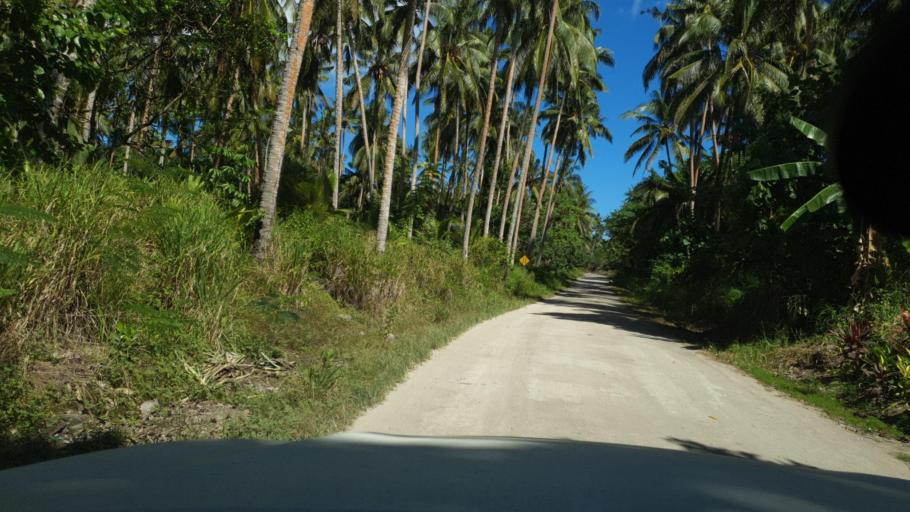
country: SB
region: Guadalcanal
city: Honiara
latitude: -9.2716
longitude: 159.6554
